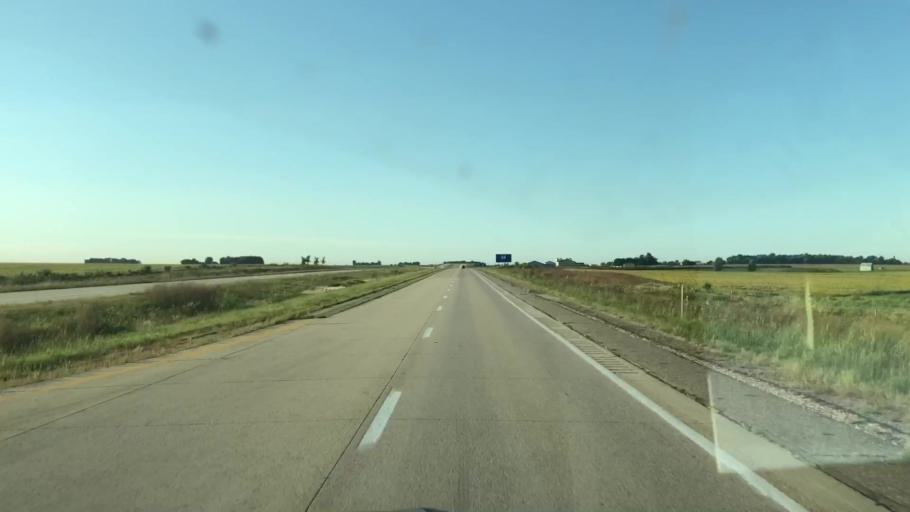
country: US
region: Iowa
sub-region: Osceola County
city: Sibley
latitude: 43.4472
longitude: -95.7136
